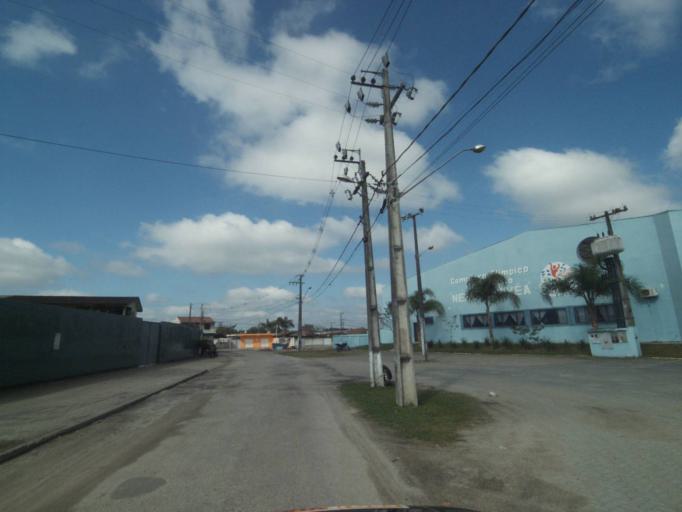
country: BR
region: Parana
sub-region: Paranagua
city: Paranagua
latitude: -25.5255
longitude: -48.5087
